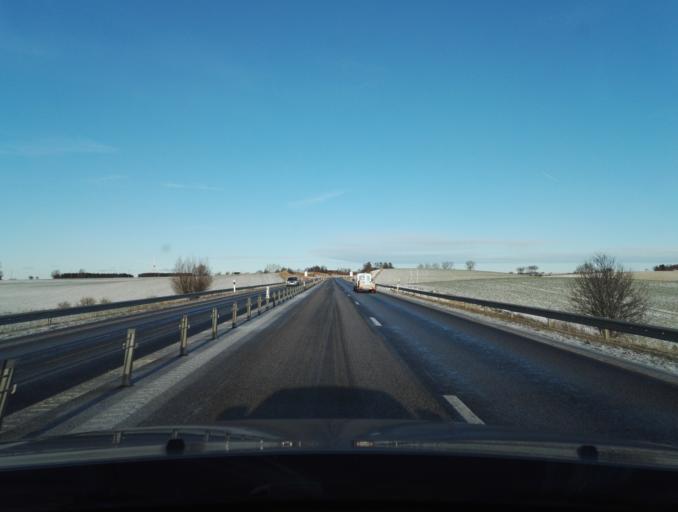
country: SE
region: Skane
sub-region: Svedala Kommun
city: Svedala
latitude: 55.4598
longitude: 13.1923
